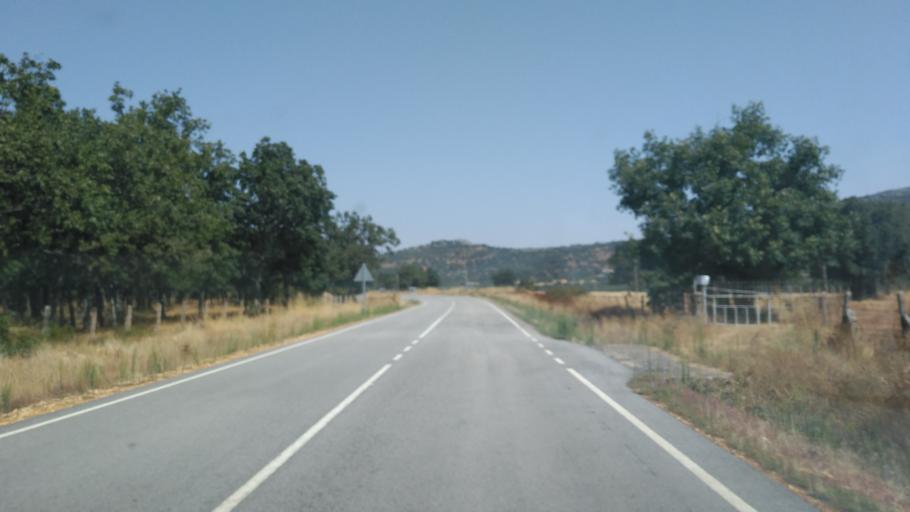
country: ES
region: Castille and Leon
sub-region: Provincia de Salamanca
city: Aldeanueva de la Sierra
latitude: 40.5927
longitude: -6.1339
